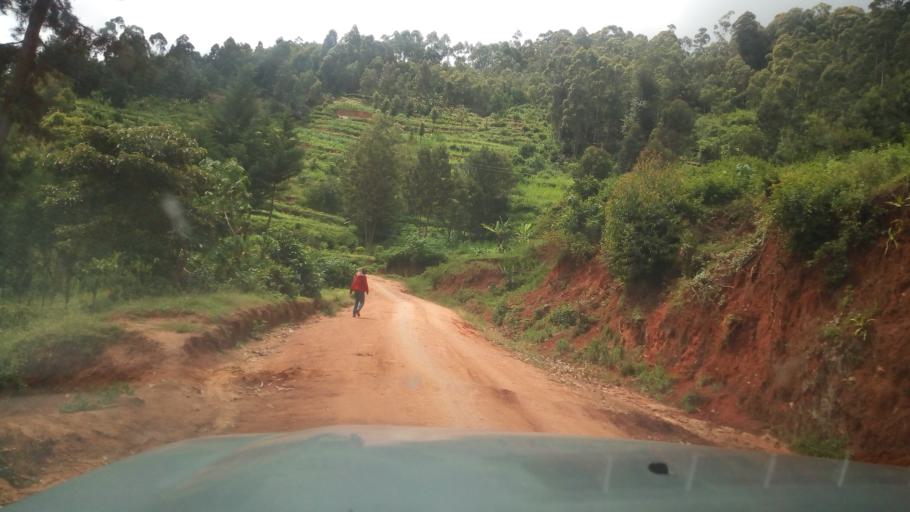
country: KE
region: Makueni
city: Wote
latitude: -1.6723
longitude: 37.4492
